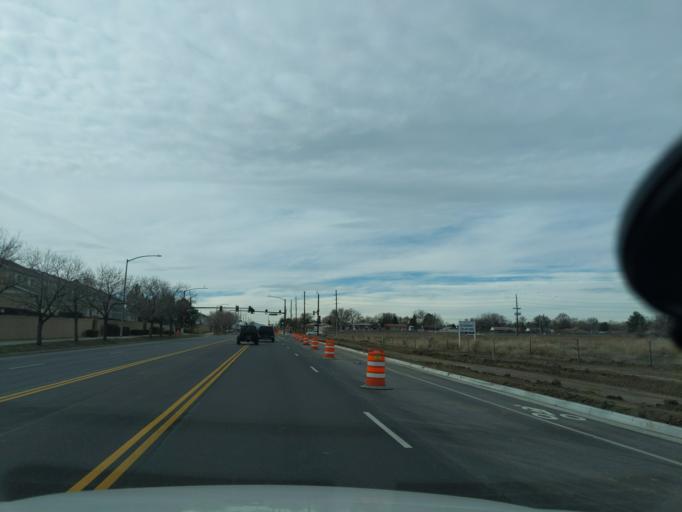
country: US
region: Colorado
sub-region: Adams County
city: Northglenn
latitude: 39.8995
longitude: -104.9572
